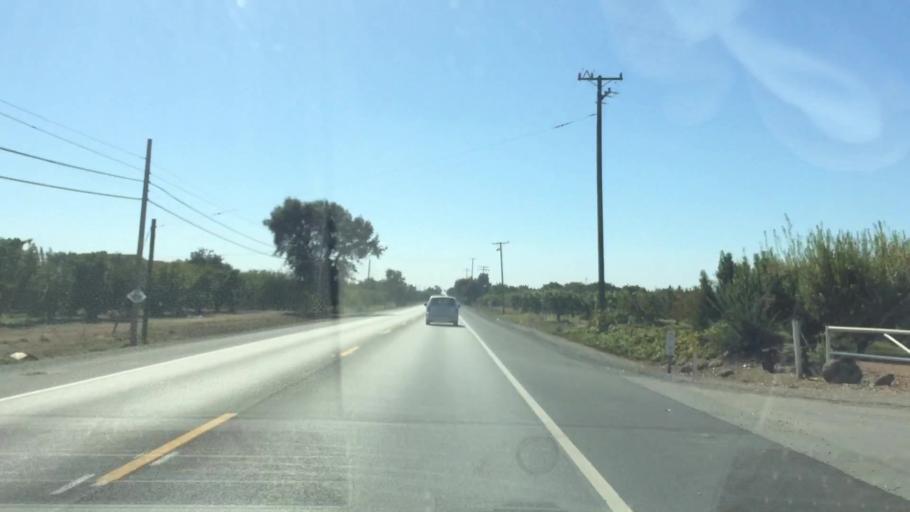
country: US
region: California
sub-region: San Joaquin County
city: Morada
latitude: 38.0200
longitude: -121.2034
